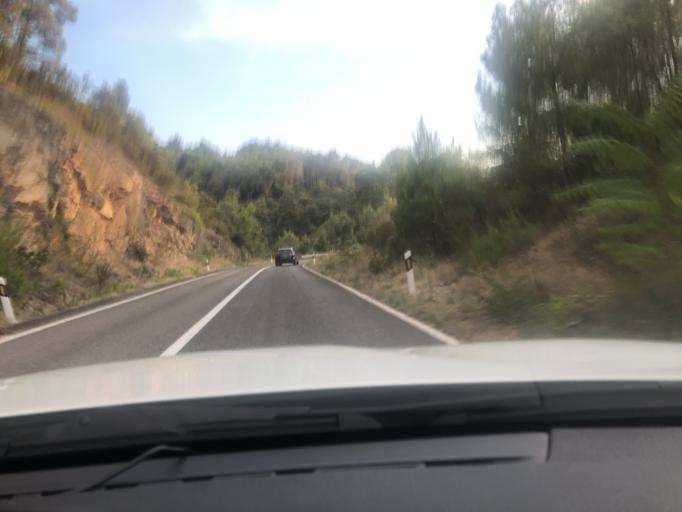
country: HR
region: Splitsko-Dalmatinska
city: Stari Grad
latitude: 43.1754
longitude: 16.5705
